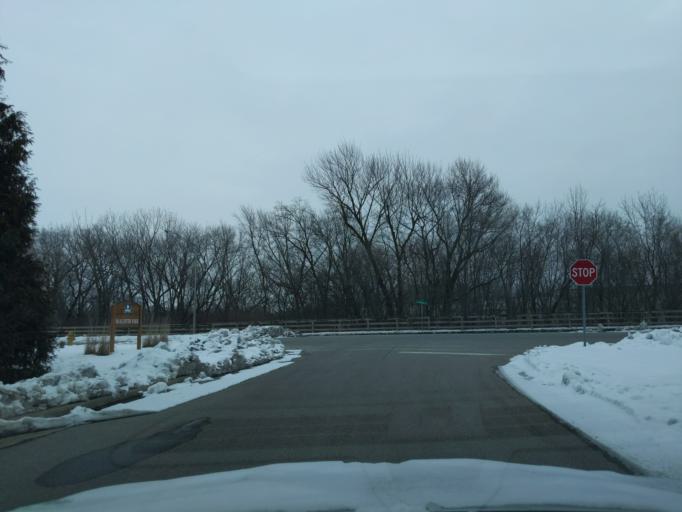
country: US
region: Indiana
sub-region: Tippecanoe County
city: Lafayette
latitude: 40.4417
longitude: -86.8848
